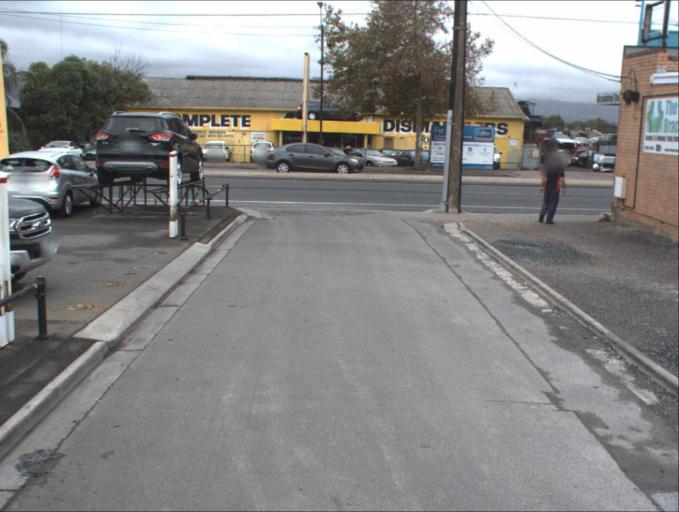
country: AU
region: South Australia
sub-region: Port Adelaide Enfield
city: Gilles Plains
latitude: -34.8618
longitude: 138.6490
